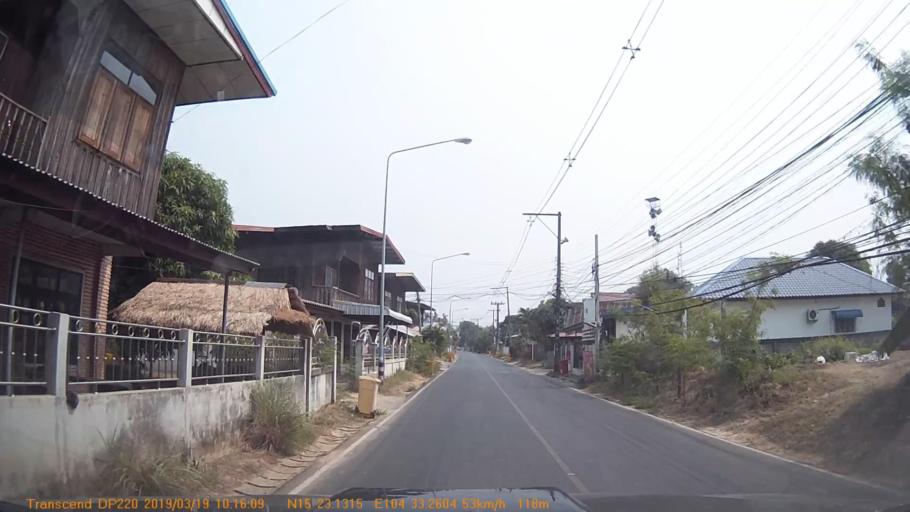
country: TH
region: Changwat Ubon Ratchathani
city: Khueang Nai
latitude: 15.3857
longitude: 104.5545
